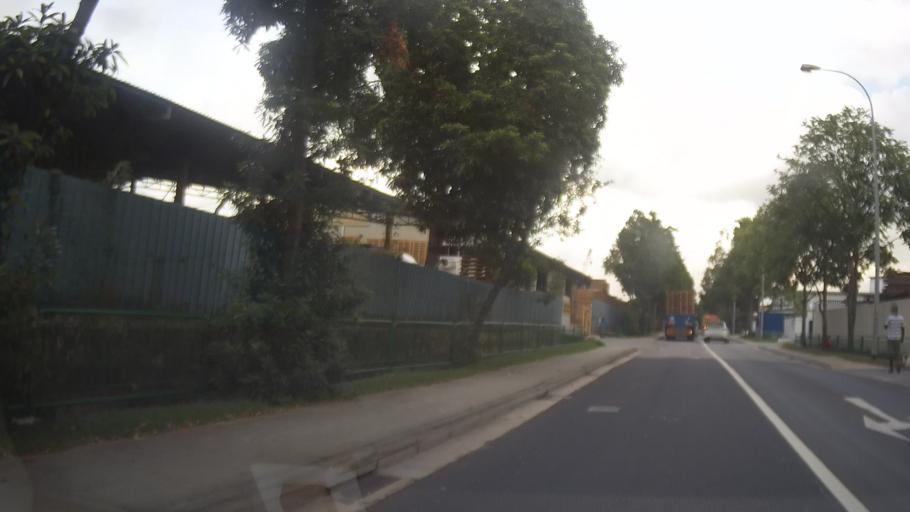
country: MY
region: Johor
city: Johor Bahru
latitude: 1.4215
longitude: 103.7500
